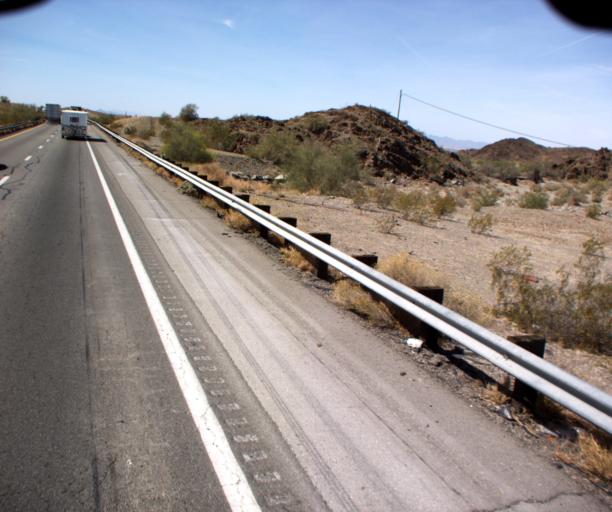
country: US
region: Arizona
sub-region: La Paz County
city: Ehrenberg
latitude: 33.6357
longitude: -114.3957
